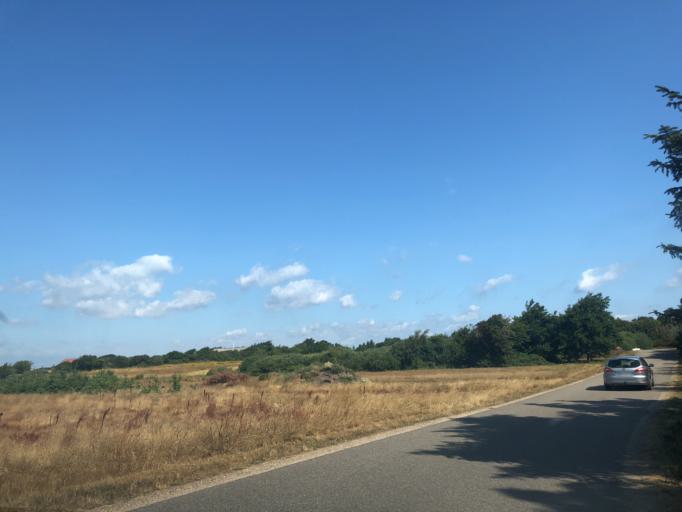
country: DK
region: North Denmark
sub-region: Morso Kommune
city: Nykobing Mors
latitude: 56.8034
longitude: 8.9977
